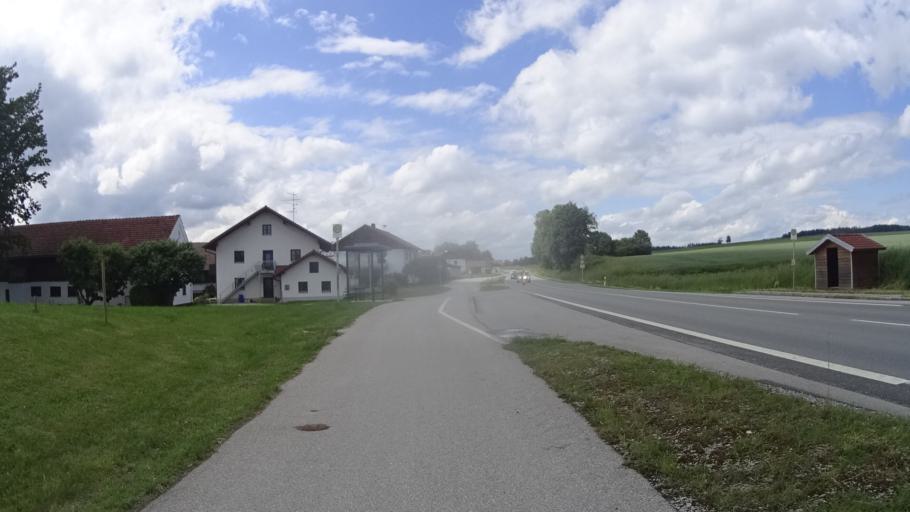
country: DE
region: Bavaria
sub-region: Lower Bavaria
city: Massing
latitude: 48.3970
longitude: 12.6335
